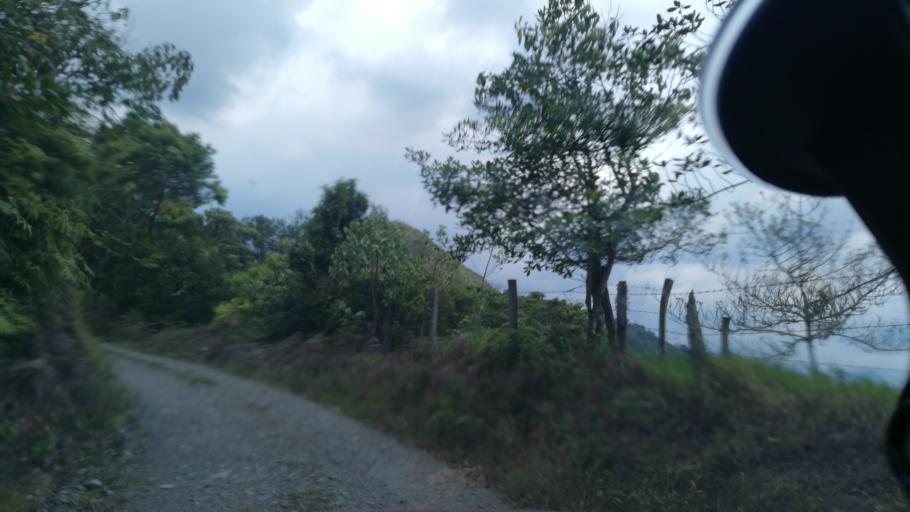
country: CO
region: Cundinamarca
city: Vergara
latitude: 5.2029
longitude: -74.2782
